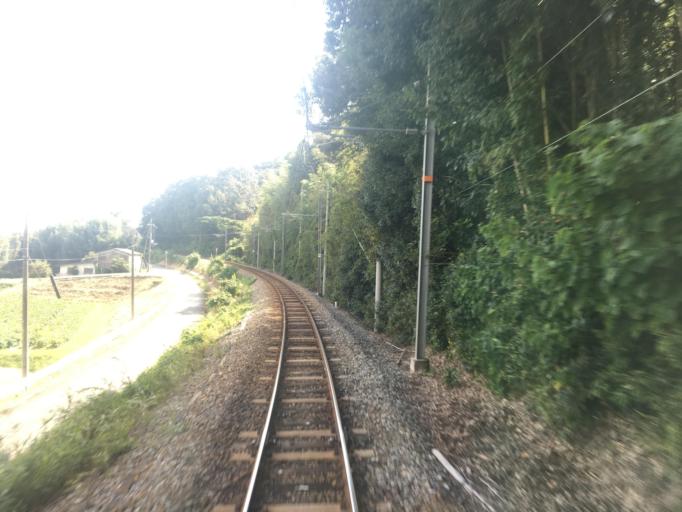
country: JP
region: Hyogo
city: Yashiro
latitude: 34.9111
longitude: 134.9264
